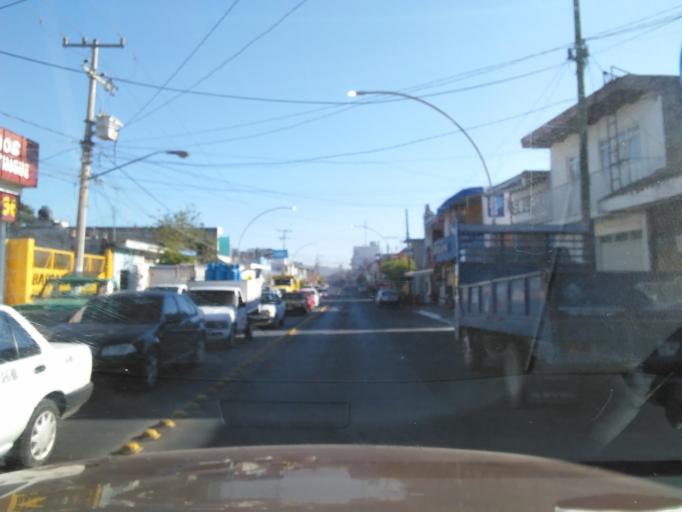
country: MX
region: Nayarit
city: Tepic
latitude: 21.5213
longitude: -104.9056
